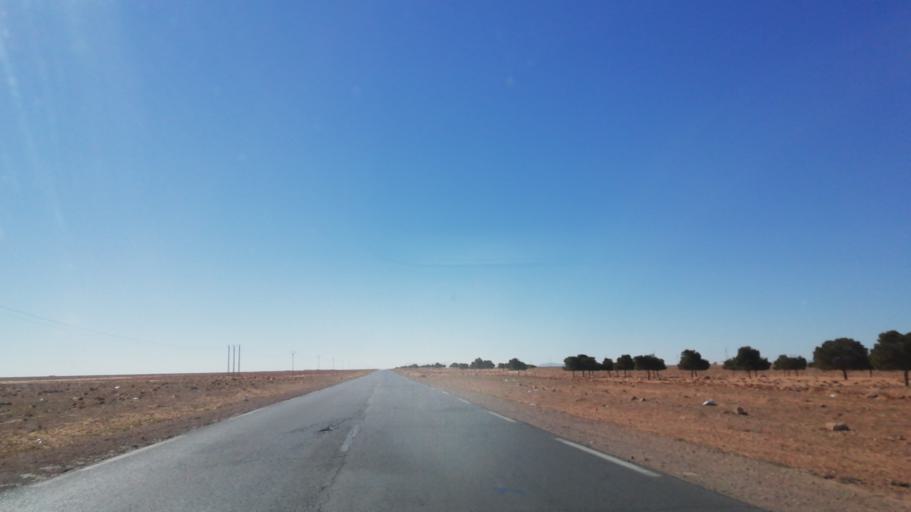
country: DZ
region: Saida
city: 'Ain el Hadjar
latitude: 33.9894
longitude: 0.0348
